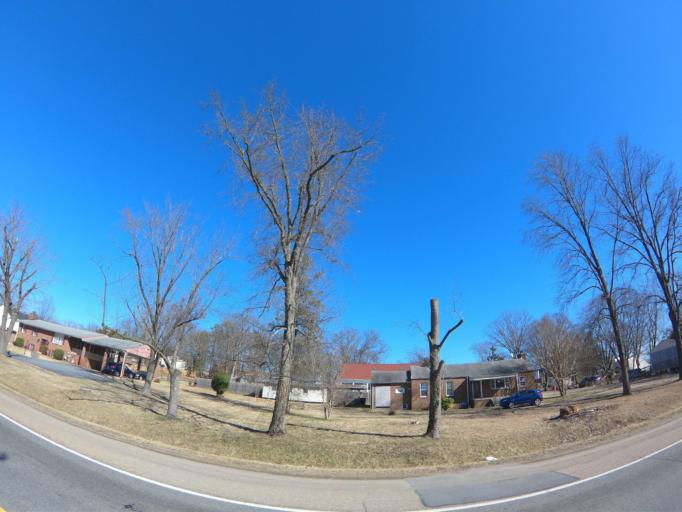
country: US
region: Maryland
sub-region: Prince George's County
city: Beltsville
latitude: 39.0388
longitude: -76.8985
